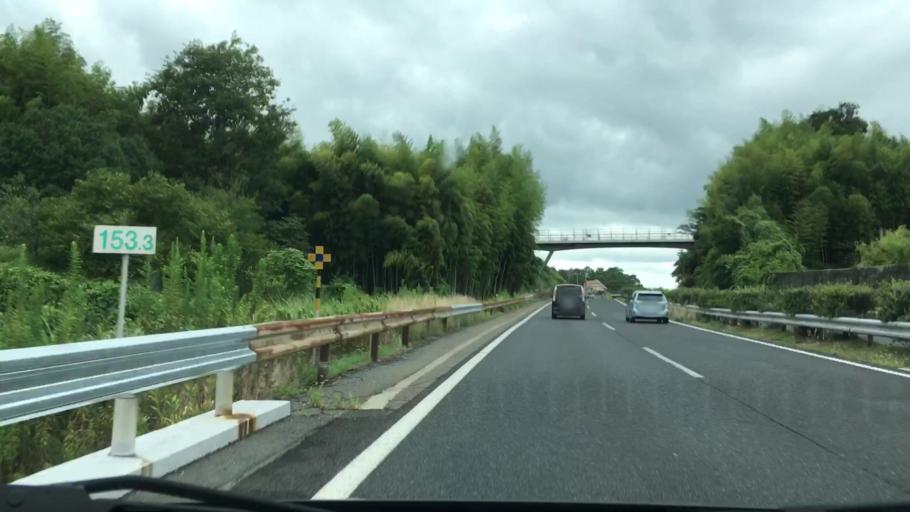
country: JP
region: Okayama
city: Tsuyama
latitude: 35.0712
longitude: 134.0279
